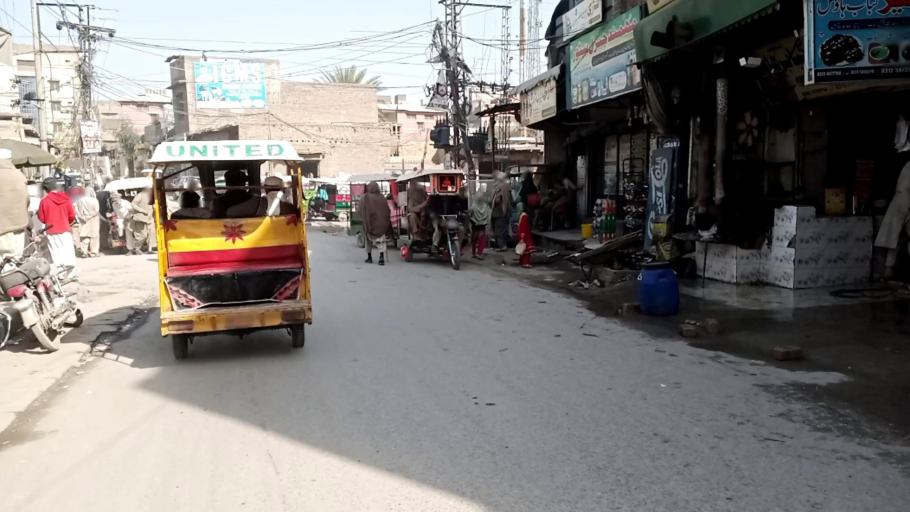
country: PK
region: Khyber Pakhtunkhwa
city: Peshawar
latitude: 34.0036
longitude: 71.5782
